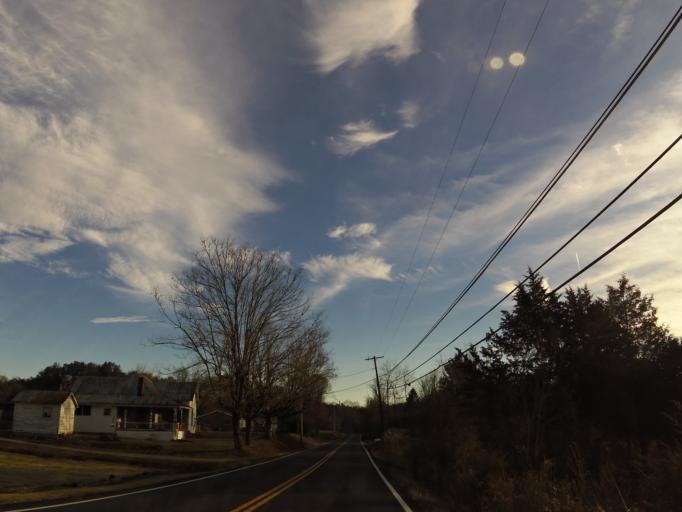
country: US
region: Tennessee
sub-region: Knox County
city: Mascot
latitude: 35.9834
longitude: -83.6945
